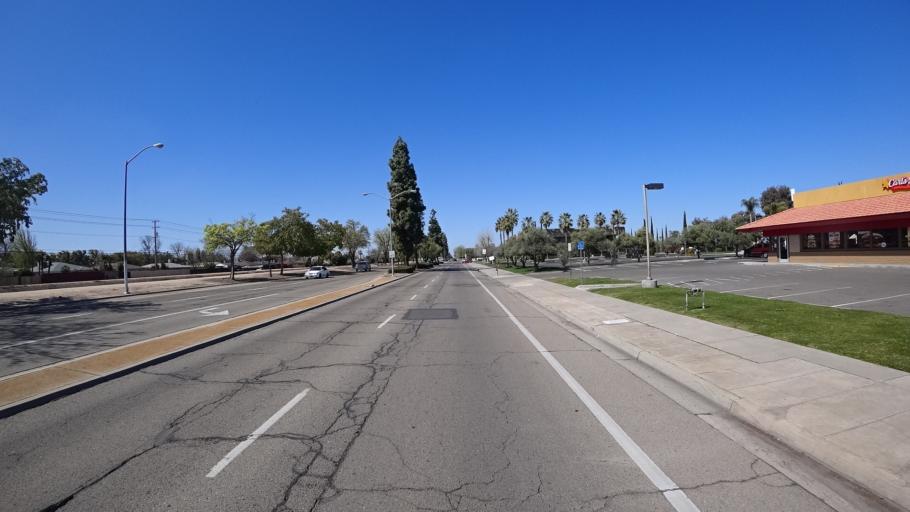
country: US
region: California
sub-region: Fresno County
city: Sunnyside
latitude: 36.7653
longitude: -119.7274
